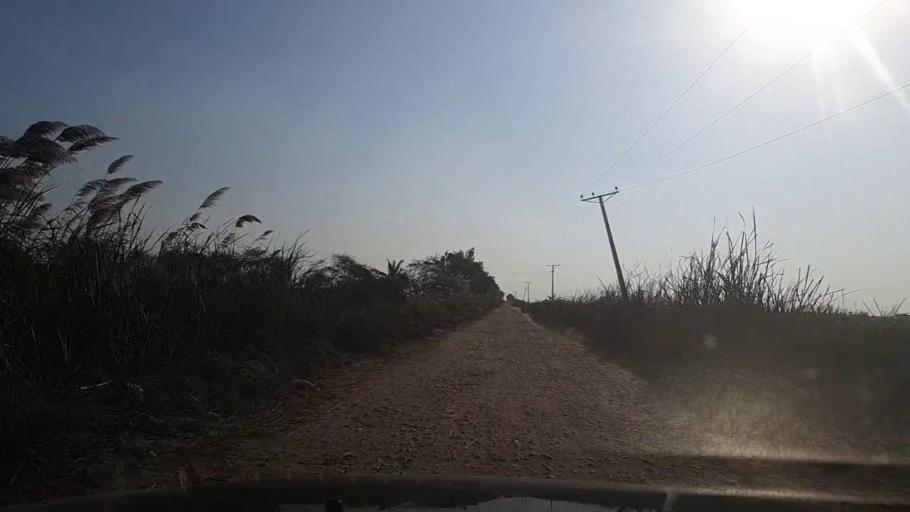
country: PK
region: Sindh
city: Gharo
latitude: 24.7240
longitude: 67.6926
